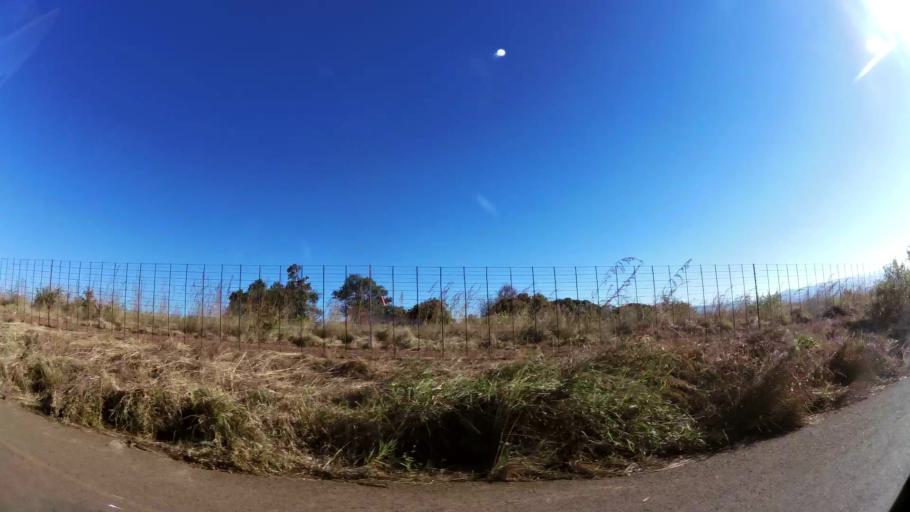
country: ZA
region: Limpopo
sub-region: Mopani District Municipality
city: Tzaneen
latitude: -23.8384
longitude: 30.1325
